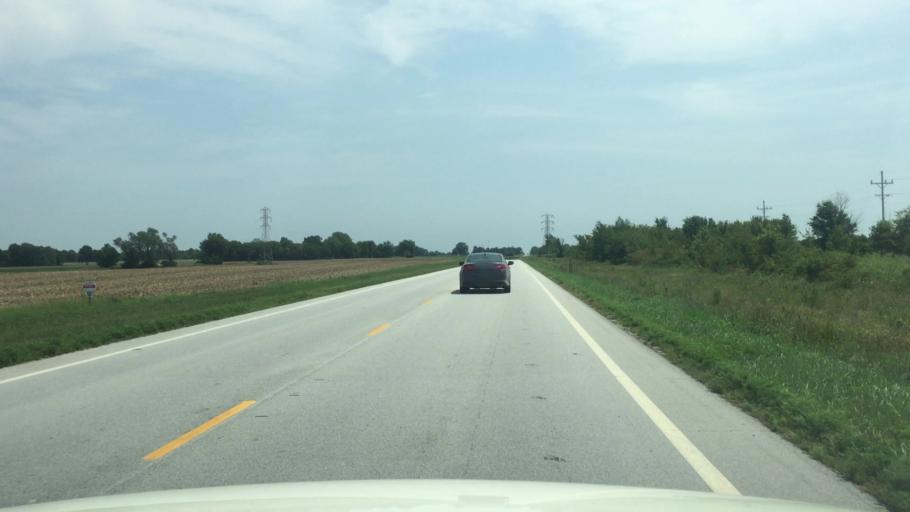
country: US
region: Kansas
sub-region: Cherokee County
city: Columbus
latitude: 37.1791
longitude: -94.9096
